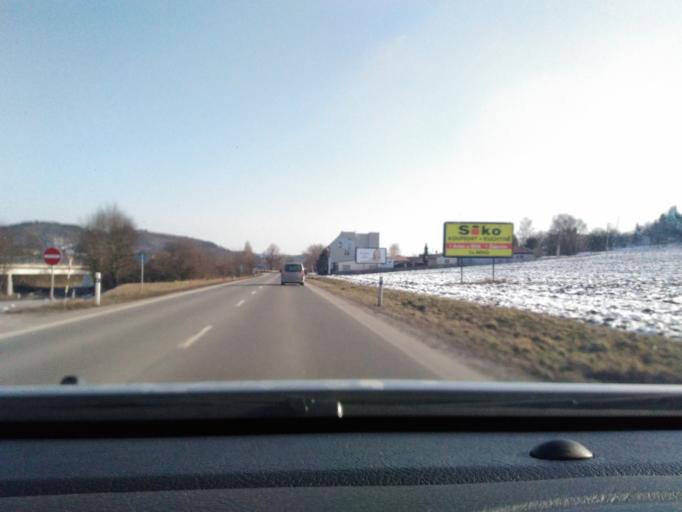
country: CZ
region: South Moravian
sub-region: Okres Brno-Venkov
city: Lelekovice
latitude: 49.2902
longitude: 16.5597
